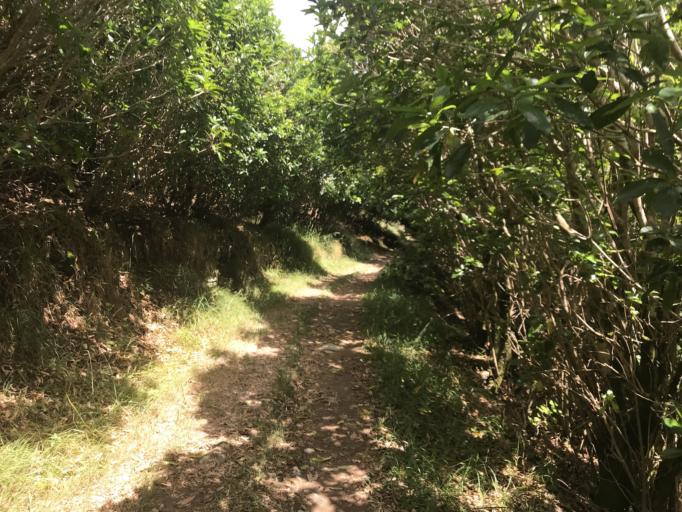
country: NZ
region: Marlborough
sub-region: Marlborough District
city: Picton
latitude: -41.2131
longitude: 174.0047
